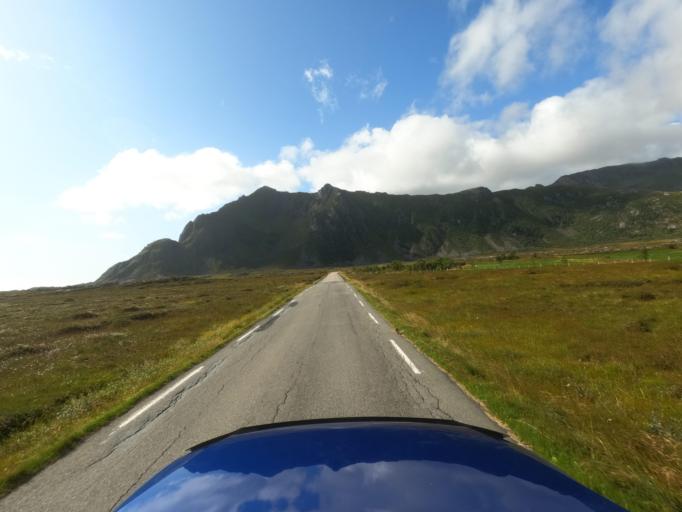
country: NO
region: Nordland
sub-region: Vestvagoy
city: Evjen
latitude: 68.2073
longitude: 14.0465
